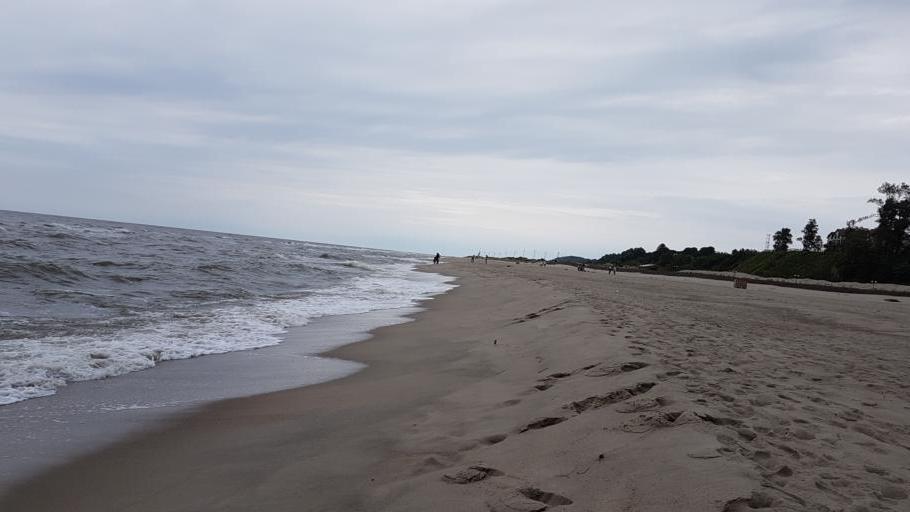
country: RU
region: Kaliningrad
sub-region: Gorod Kaliningrad
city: Yantarnyy
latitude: 54.8711
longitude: 19.9321
